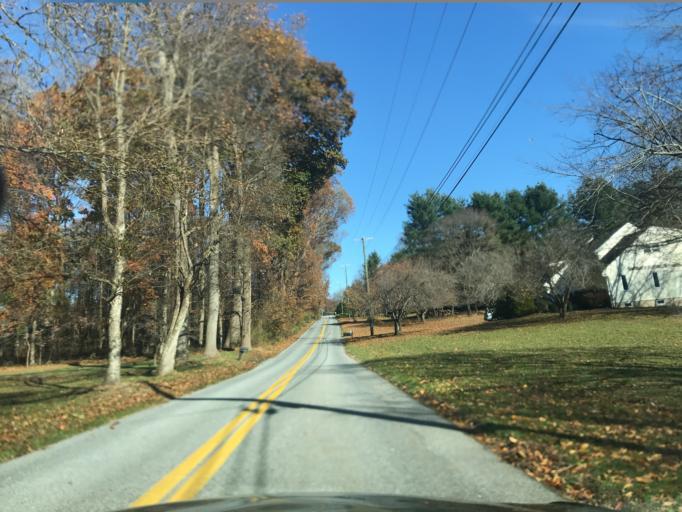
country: US
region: Maryland
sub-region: Baltimore County
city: Hunt Valley
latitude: 39.5102
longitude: -76.5482
